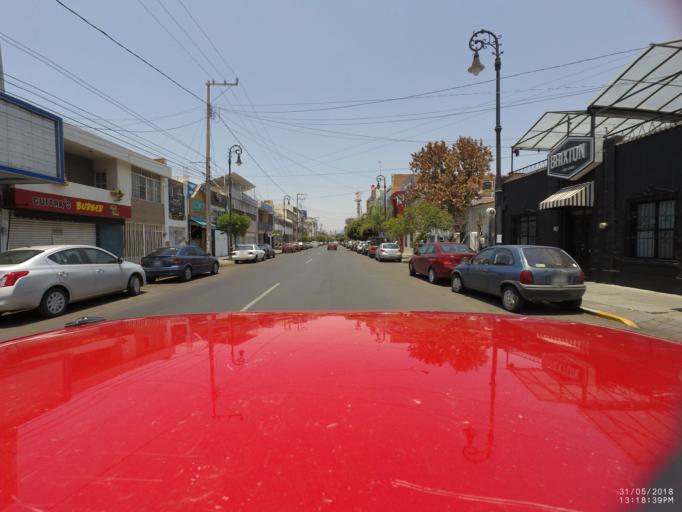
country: MX
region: Aguascalientes
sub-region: Aguascalientes
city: Aguascalientes
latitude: 21.8834
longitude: -102.2880
